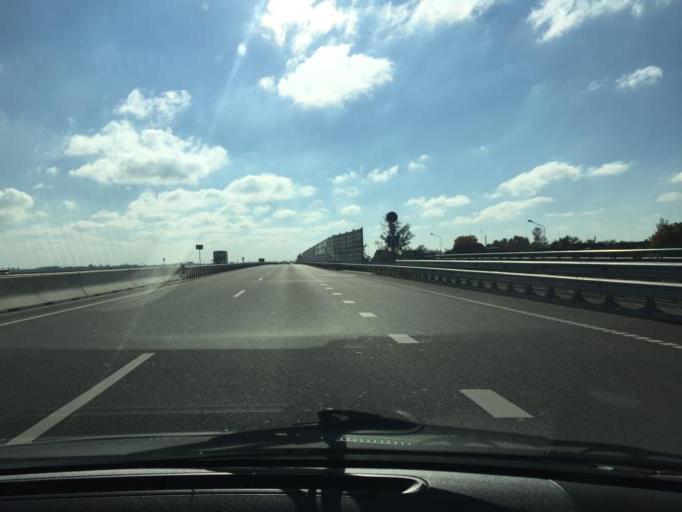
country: BY
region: Minsk
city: Slutsk
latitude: 53.1465
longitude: 27.5519
